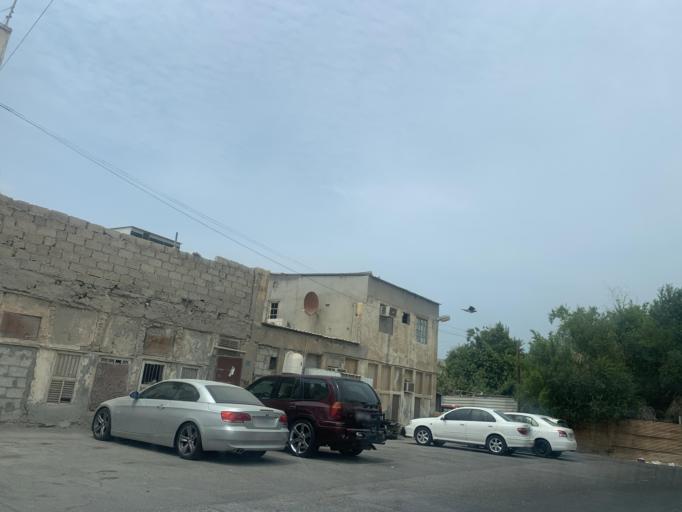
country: BH
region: Muharraq
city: Al Muharraq
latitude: 26.2823
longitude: 50.6352
